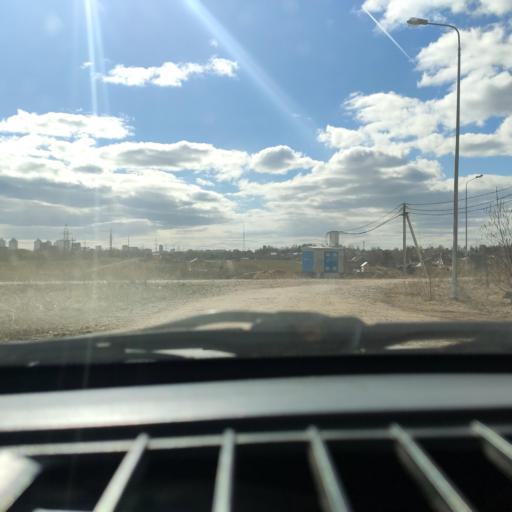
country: RU
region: Perm
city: Perm
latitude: 58.0239
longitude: 56.3520
